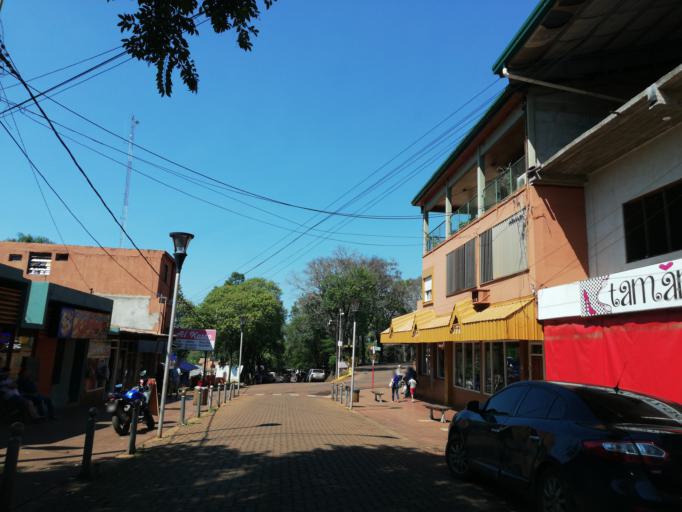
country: AR
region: Misiones
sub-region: Departamento de Eldorado
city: Eldorado
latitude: -26.4105
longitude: -54.6062
